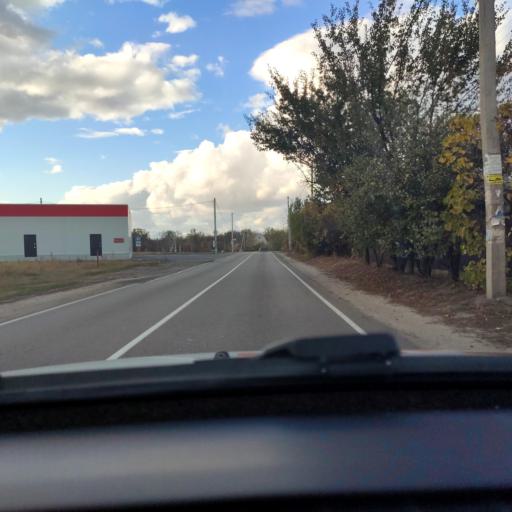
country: RU
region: Voronezj
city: Ramon'
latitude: 51.8258
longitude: 39.2569
